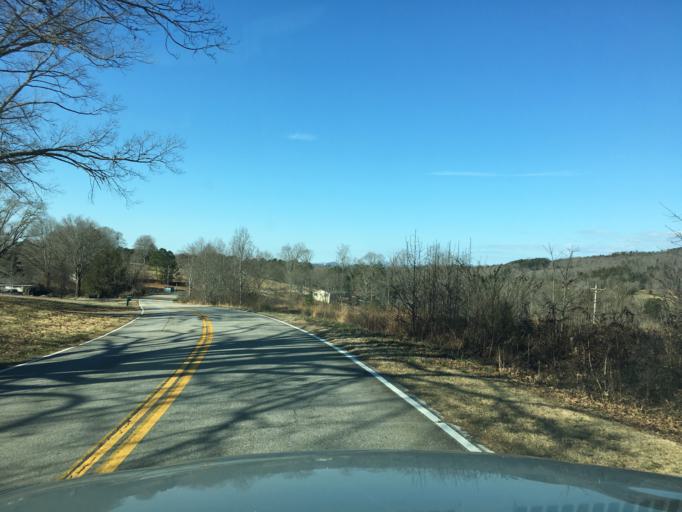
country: US
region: South Carolina
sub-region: Pickens County
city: Pickens
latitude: 34.8756
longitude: -82.6691
